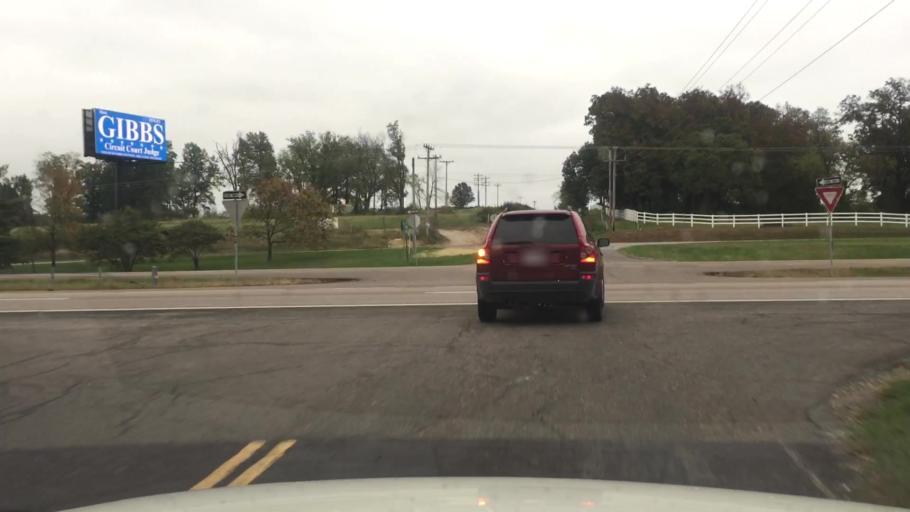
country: US
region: Missouri
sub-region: Boone County
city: Ashland
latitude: 38.8106
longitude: -92.2517
